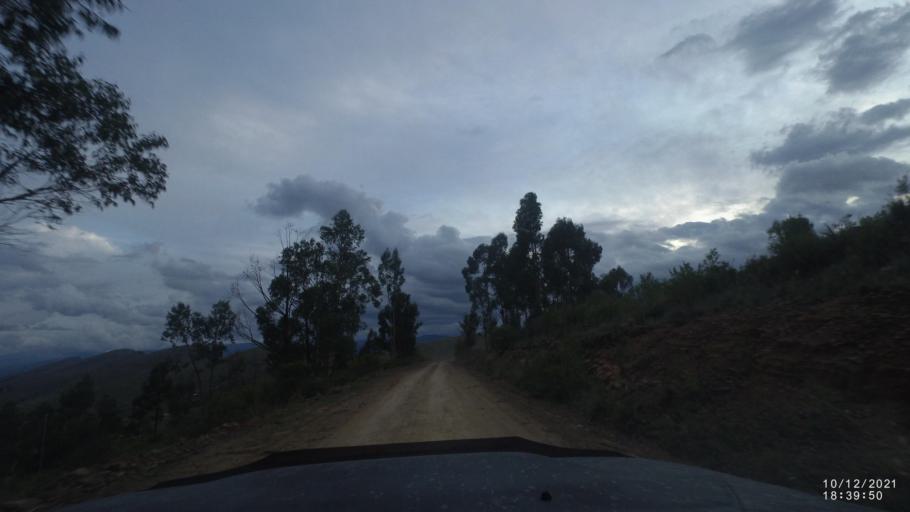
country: BO
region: Cochabamba
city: Tarata
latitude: -17.8529
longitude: -65.9879
